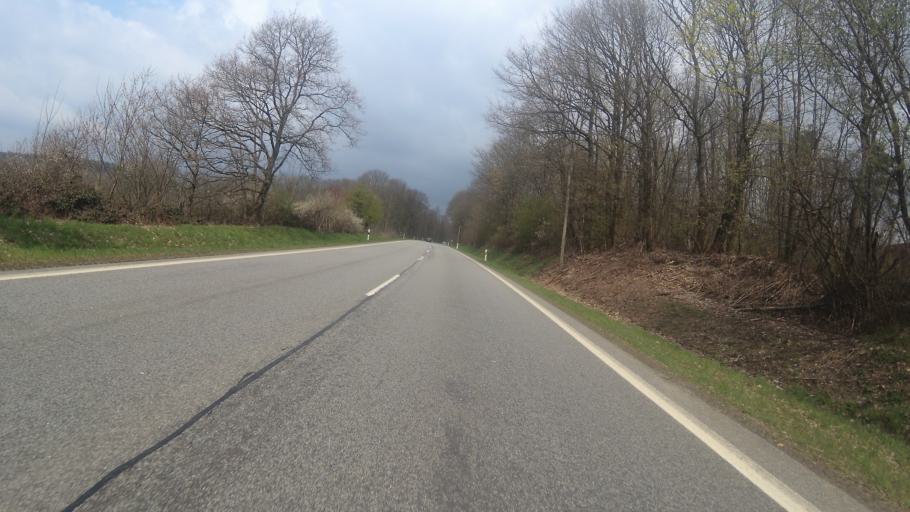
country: DE
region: Saarland
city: Nonnweiler
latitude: 49.6153
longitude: 6.9638
